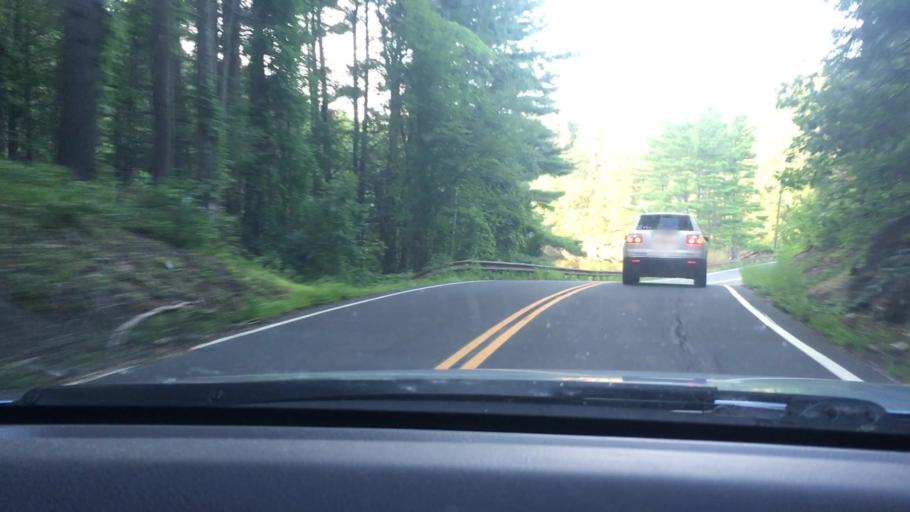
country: US
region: Connecticut
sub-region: Fairfield County
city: Georgetown
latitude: 41.2851
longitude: -73.3882
